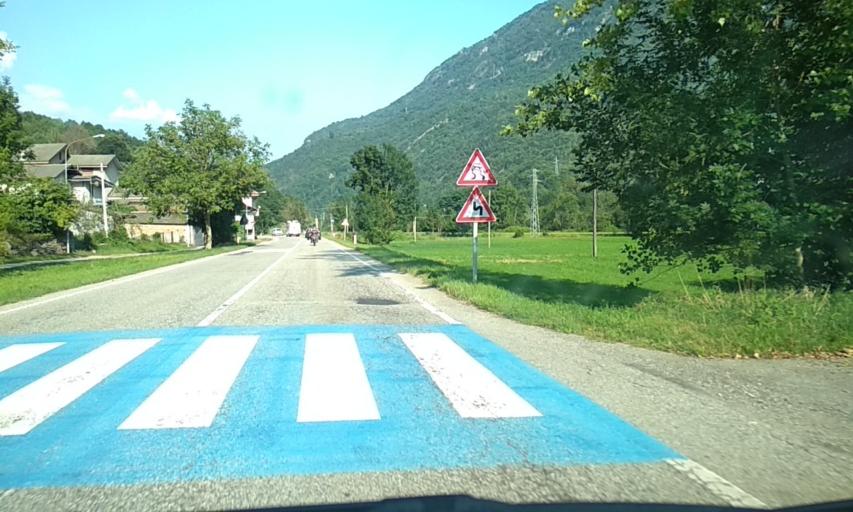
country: IT
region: Piedmont
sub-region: Provincia di Torino
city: Sparone
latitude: 45.4088
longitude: 7.5317
